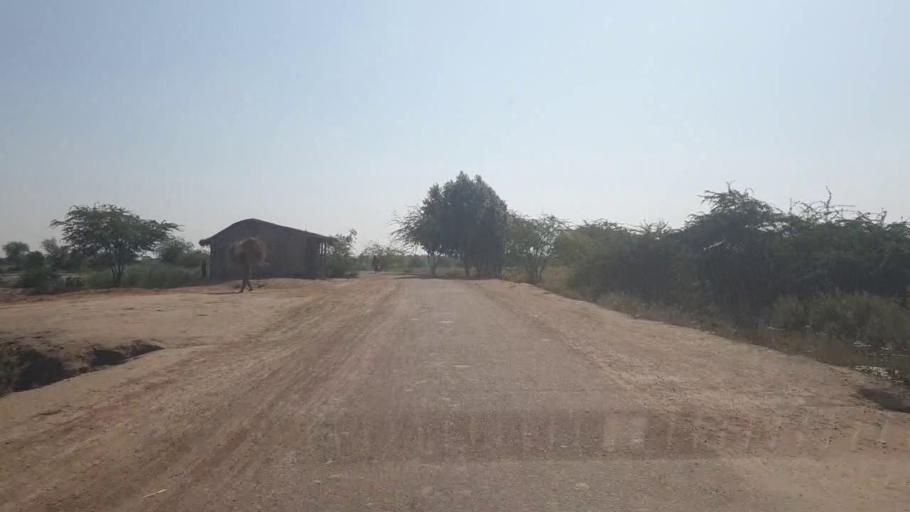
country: PK
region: Sindh
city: Badin
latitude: 24.5907
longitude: 68.8455
